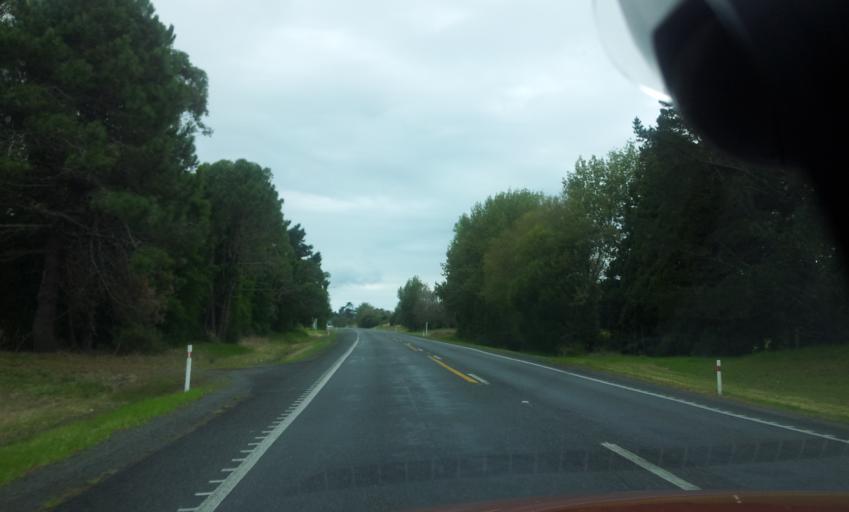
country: NZ
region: Northland
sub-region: Whangarei
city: Ruakaka
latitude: -35.9572
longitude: 174.4508
